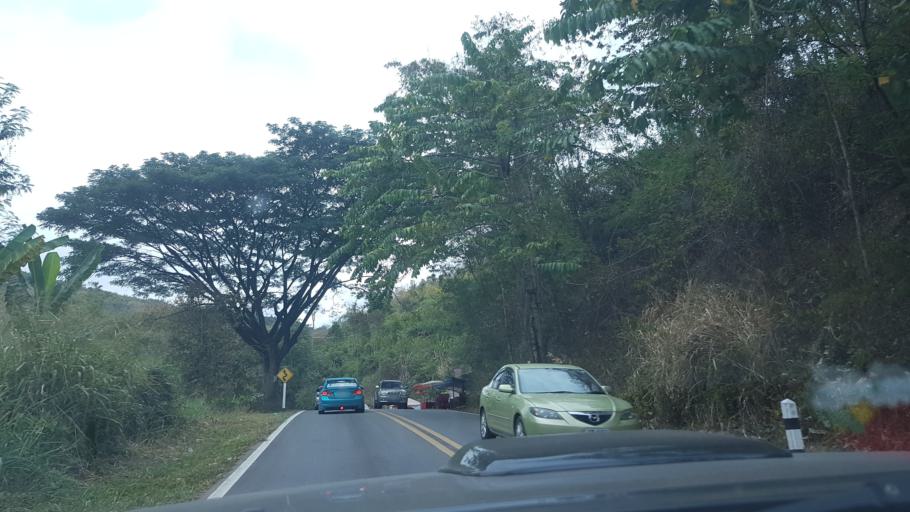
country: TH
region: Phetchabun
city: Khao Kho
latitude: 16.5440
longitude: 101.0436
